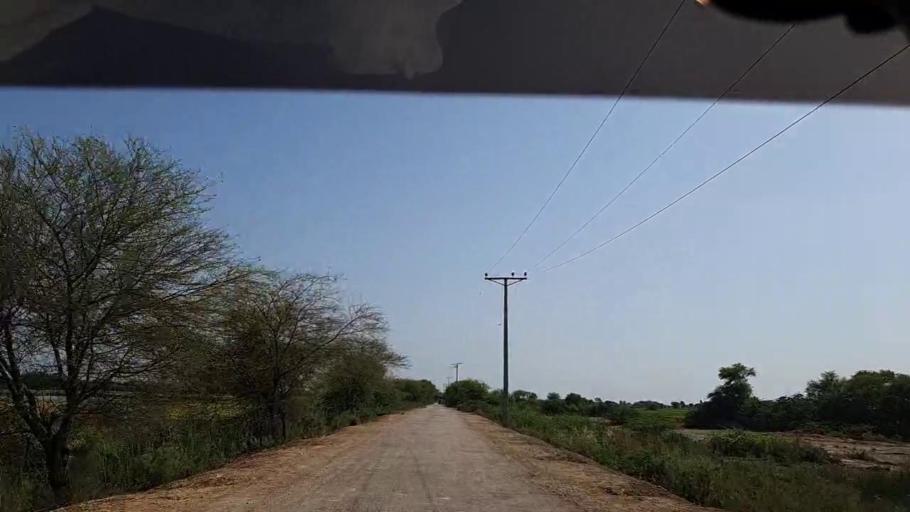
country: PK
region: Sindh
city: Badin
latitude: 24.6487
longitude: 68.7876
